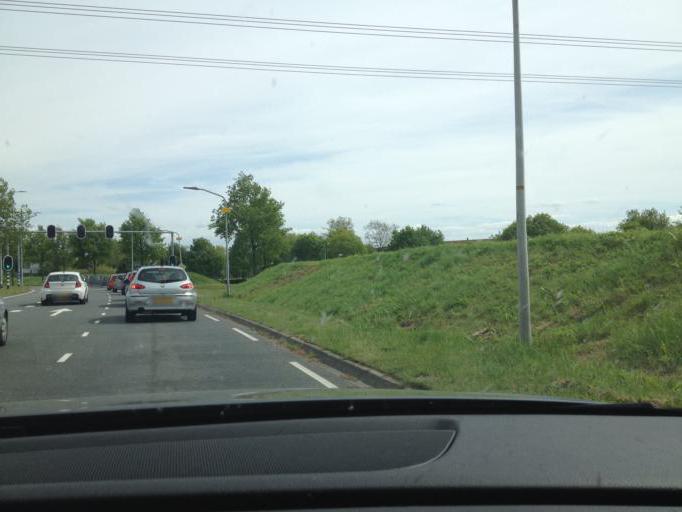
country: NL
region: Flevoland
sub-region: Gemeente Almere
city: Almere Stad
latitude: 52.3686
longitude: 5.2404
